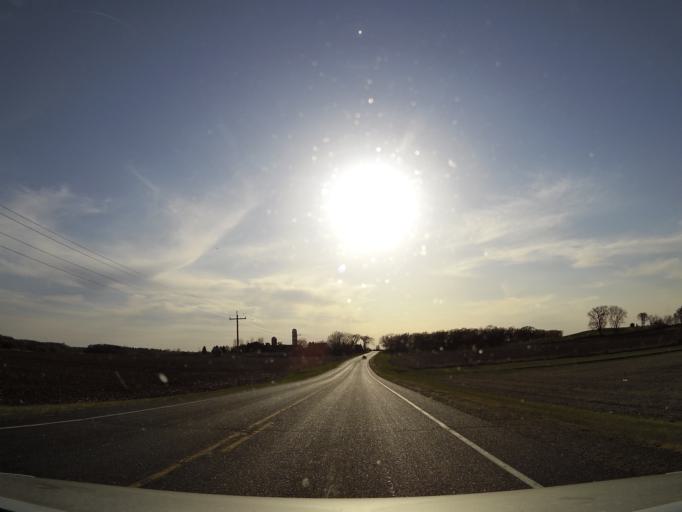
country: US
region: Wisconsin
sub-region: Pierce County
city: River Falls
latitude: 44.8244
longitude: -92.7141
